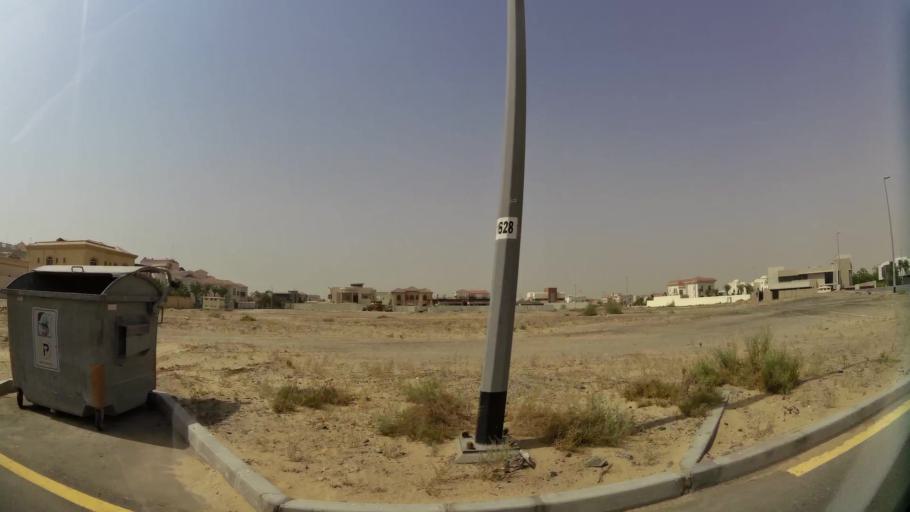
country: AE
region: Ash Shariqah
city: Sharjah
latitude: 25.2465
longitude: 55.4880
